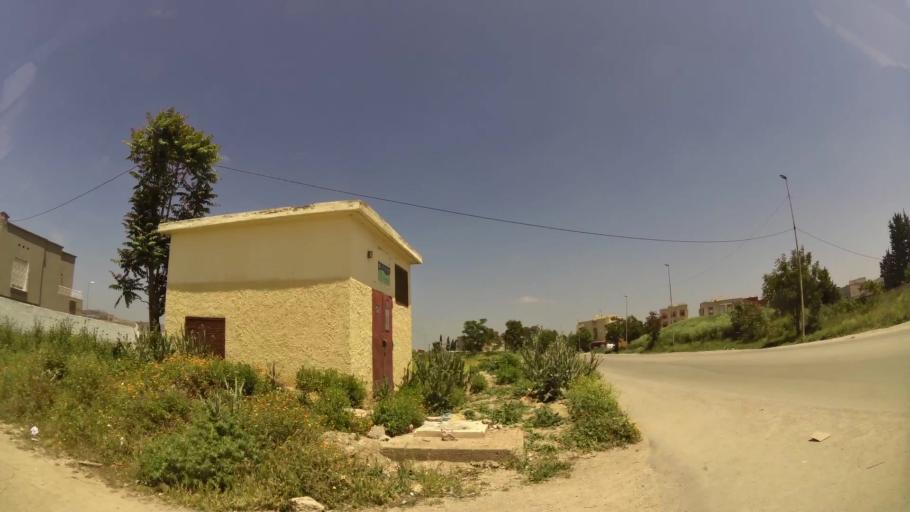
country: MA
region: Fes-Boulemane
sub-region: Fes
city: Fes
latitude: 34.0374
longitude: -5.0429
